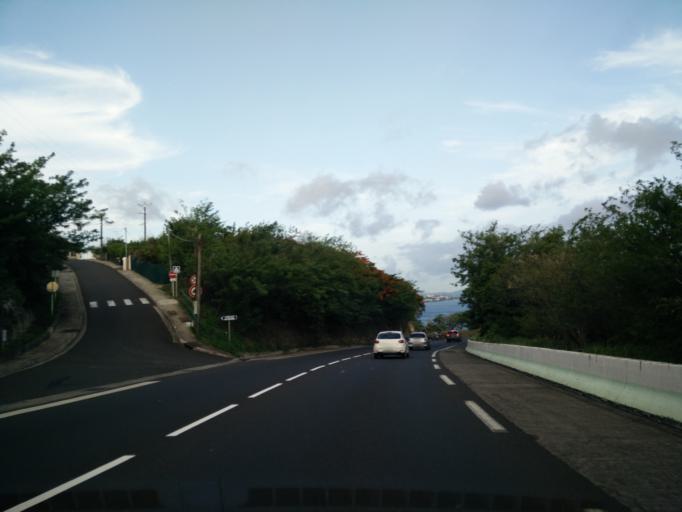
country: MQ
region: Martinique
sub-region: Martinique
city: Fort-de-France
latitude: 14.6308
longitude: -61.1236
